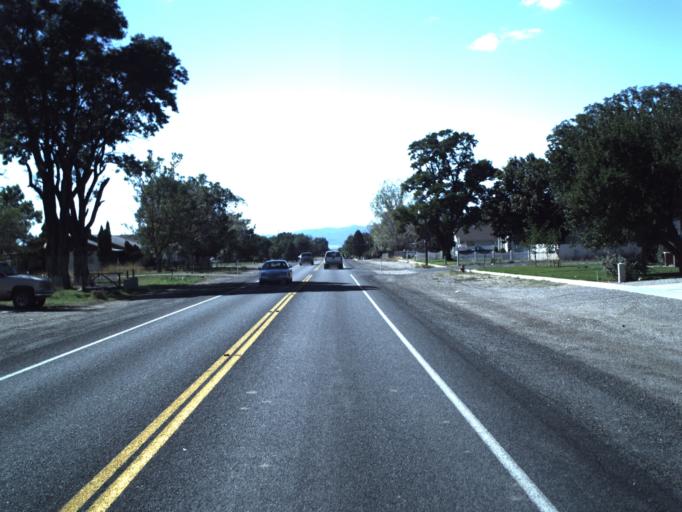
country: US
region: Utah
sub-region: Beaver County
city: Beaver
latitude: 38.2771
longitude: -112.6231
